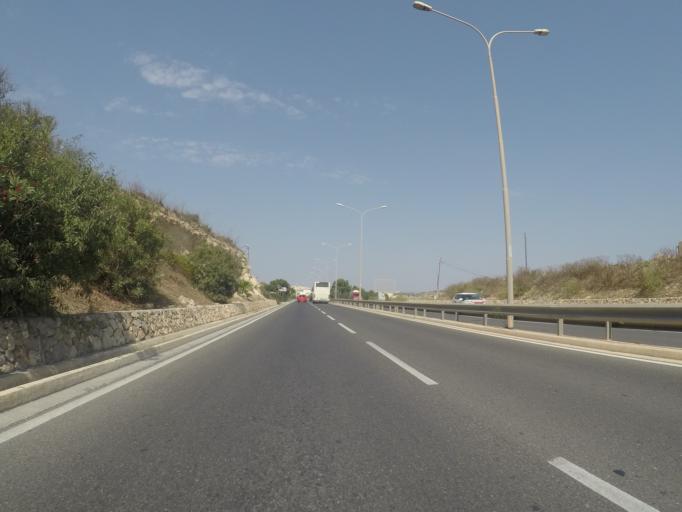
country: MT
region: Saint Paul's Bay
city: San Pawl il-Bahar
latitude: 35.9462
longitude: 14.4036
